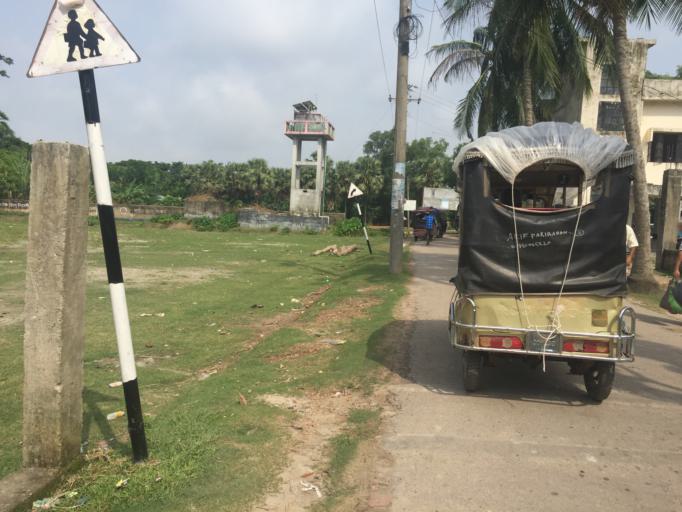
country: BD
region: Barisal
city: Mathba
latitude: 22.2451
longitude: 89.9136
